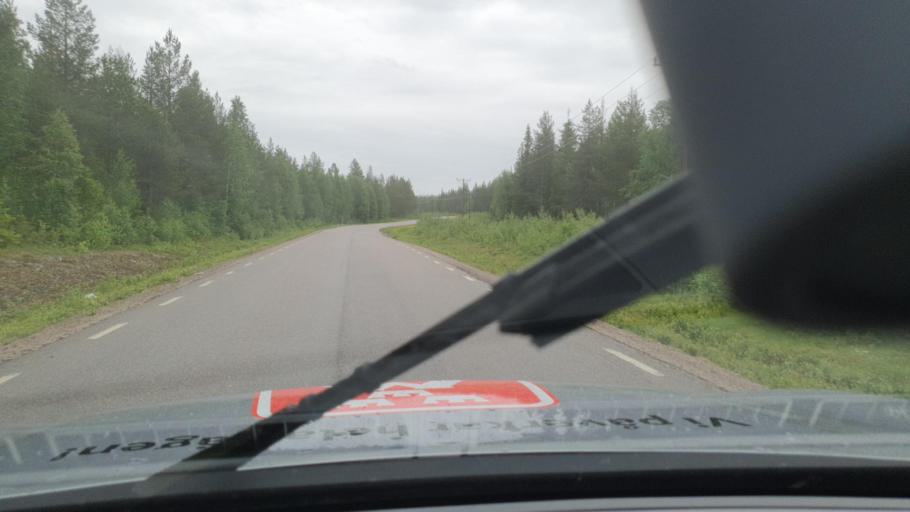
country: SE
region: Norrbotten
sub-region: Pajala Kommun
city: Pajala
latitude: 66.7700
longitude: 23.1468
